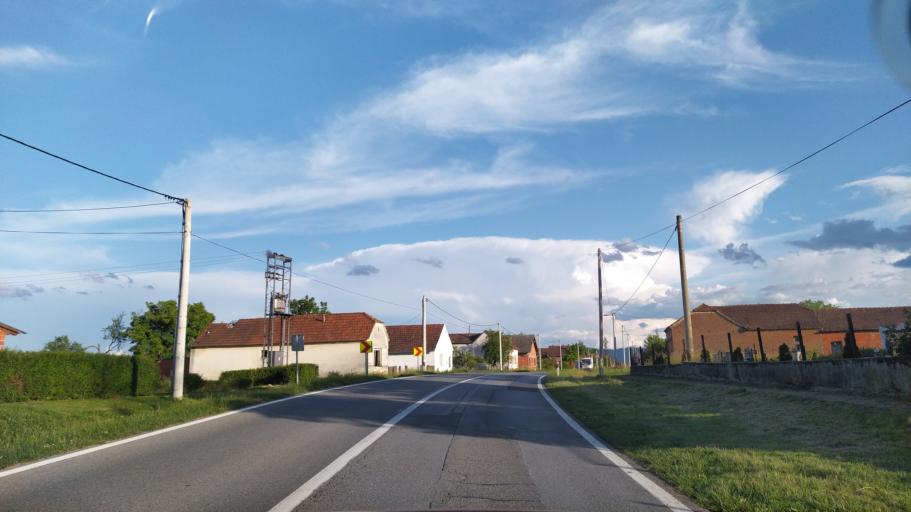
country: HR
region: Virovitick-Podravska
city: Cacinci
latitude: 45.6312
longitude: 17.7974
